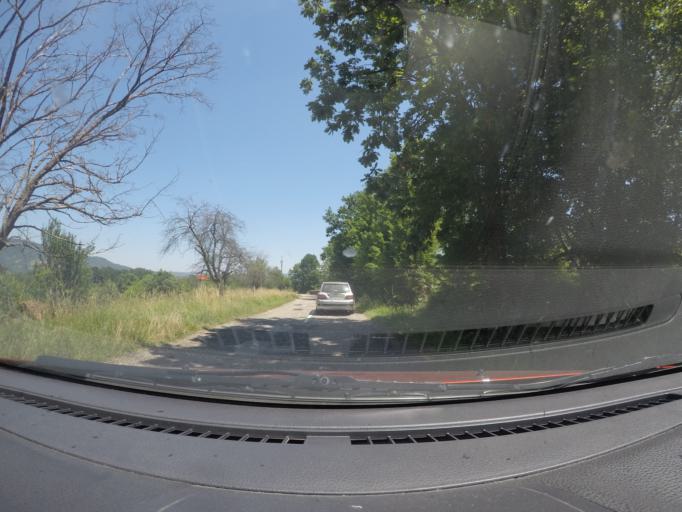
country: RO
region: Mehedinti
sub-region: Comuna Svinita
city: Svinita
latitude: 44.4703
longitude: 22.0956
